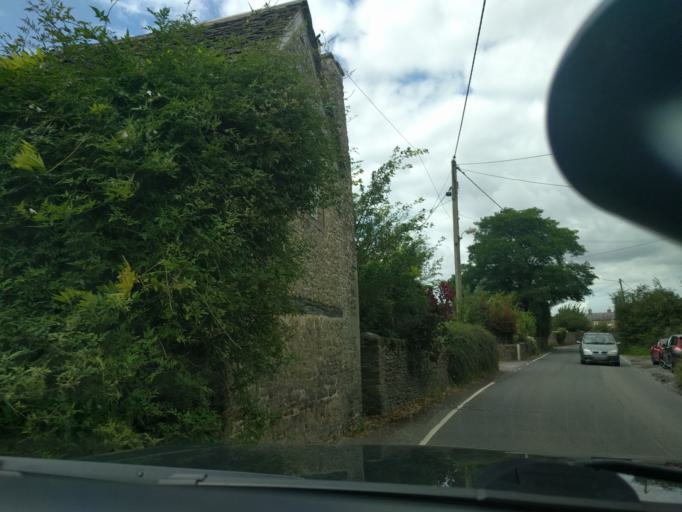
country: GB
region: England
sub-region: Wiltshire
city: Corsham
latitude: 51.4196
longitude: -2.1773
